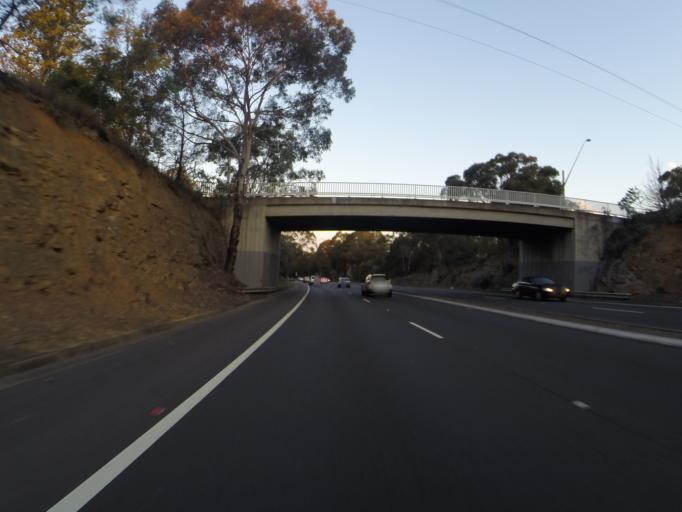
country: AU
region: New South Wales
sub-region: Blue Mountains Municipality
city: Glenbrook
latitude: -33.7609
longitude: 150.6136
